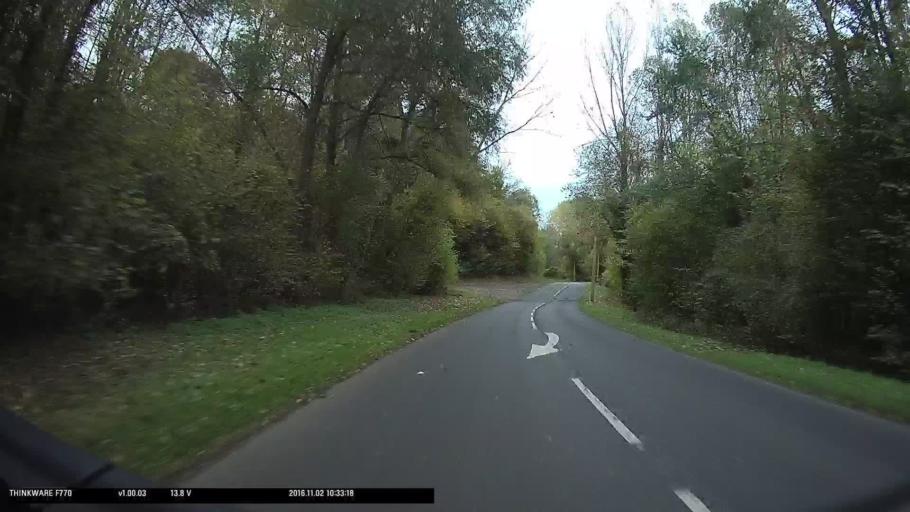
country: FR
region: Ile-de-France
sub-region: Departement du Val-d'Oise
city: Ableiges
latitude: 49.0870
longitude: 1.9935
